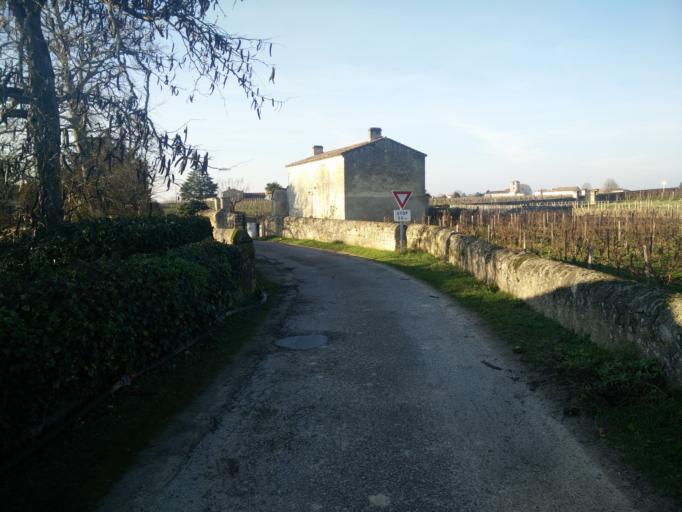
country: FR
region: Aquitaine
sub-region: Departement de la Gironde
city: Saint-Emilion
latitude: 44.8885
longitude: -0.1608
